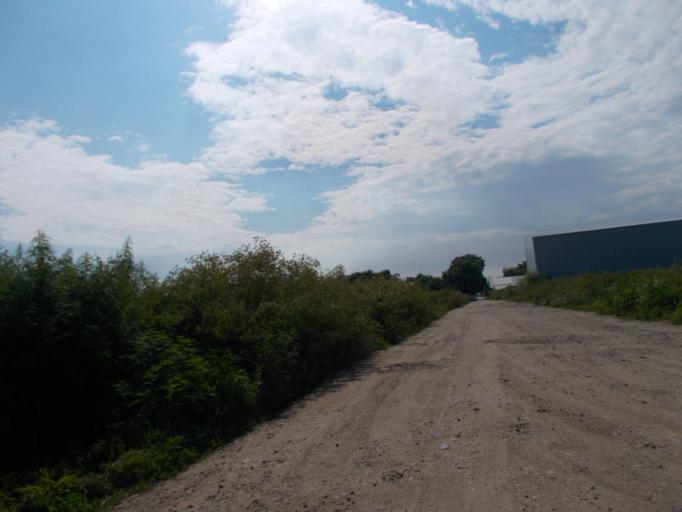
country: RO
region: Ilfov
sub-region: Comuna Jilava
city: Jilava
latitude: 44.3287
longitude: 26.0679
